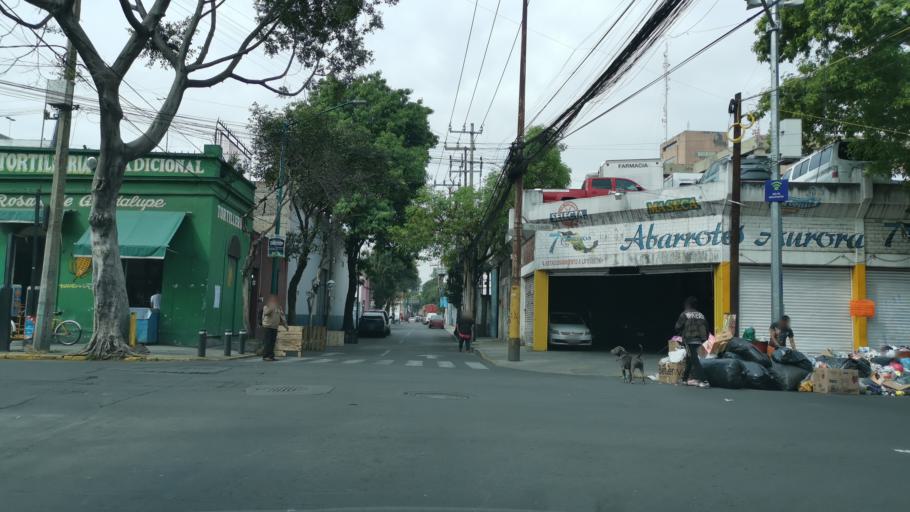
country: MX
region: Mexico City
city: Mexico City
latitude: 19.4213
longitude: -99.1294
